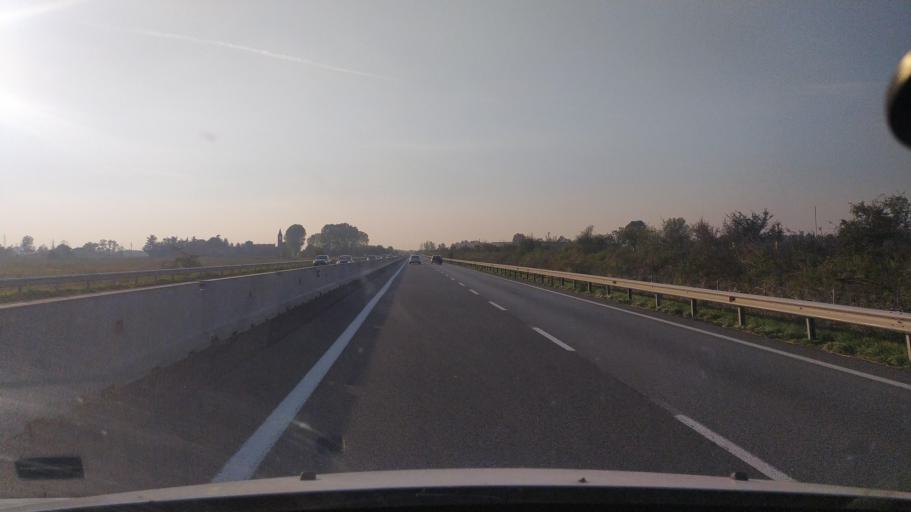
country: IT
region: Lombardy
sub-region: Provincia di Cremona
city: Nosadello
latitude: 45.3900
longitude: 9.5182
